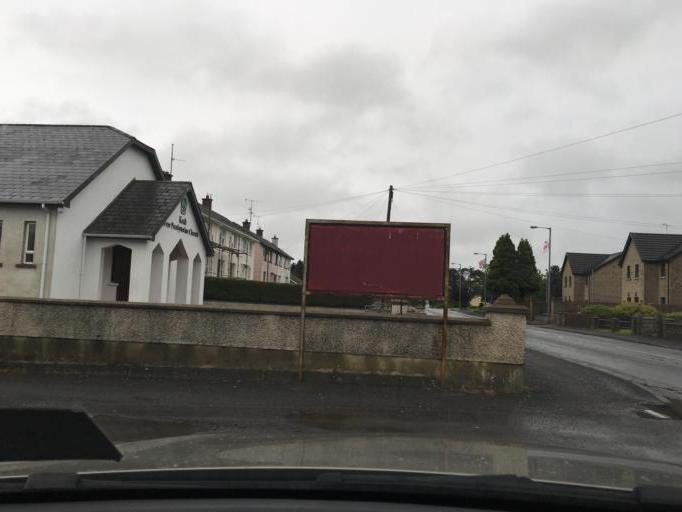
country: GB
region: Northern Ireland
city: Irvinestown
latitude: 54.5229
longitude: -7.7214
